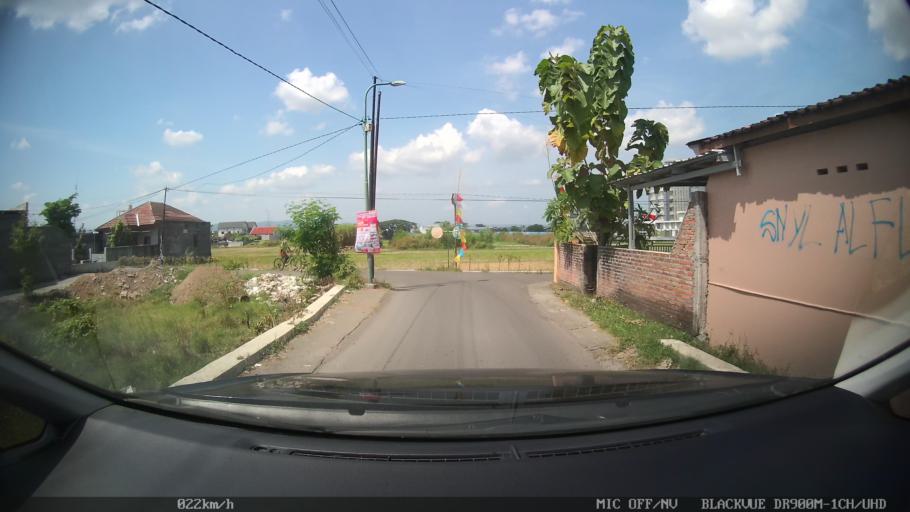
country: ID
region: Daerah Istimewa Yogyakarta
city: Sewon
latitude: -7.8308
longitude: 110.3847
